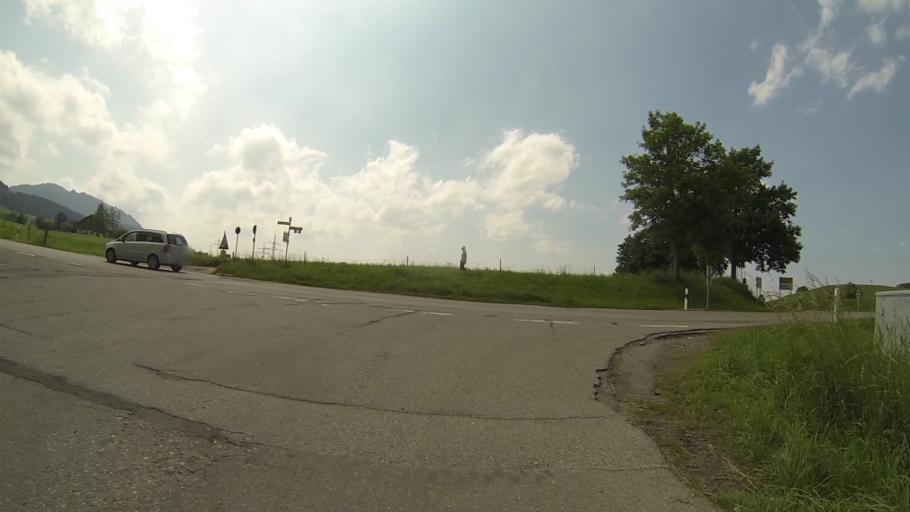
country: DE
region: Bavaria
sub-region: Swabia
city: Nesselwang
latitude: 47.6225
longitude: 10.4936
